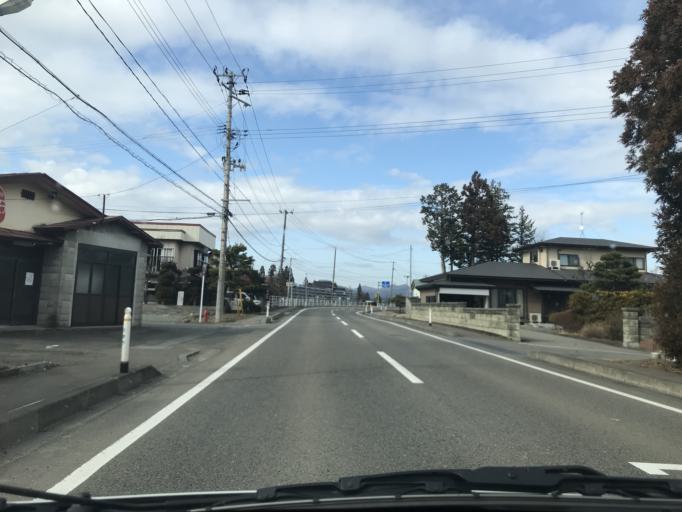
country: JP
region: Iwate
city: Hanamaki
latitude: 39.3623
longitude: 141.0509
